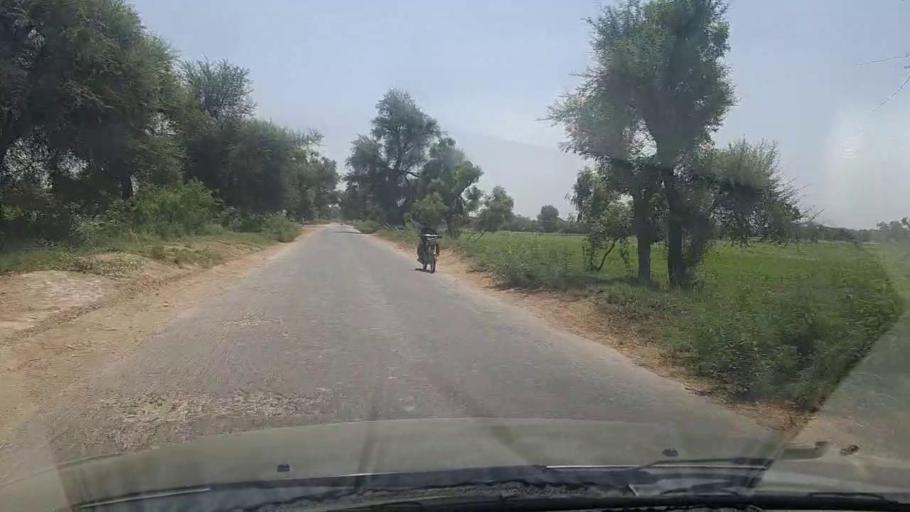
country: PK
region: Sindh
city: Tando Jam
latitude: 25.2825
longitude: 68.6036
